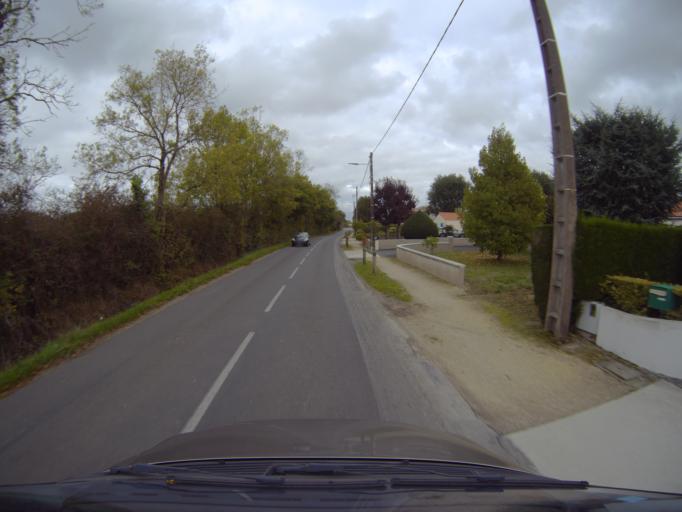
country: FR
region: Pays de la Loire
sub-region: Departement de la Loire-Atlantique
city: Clisson
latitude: 47.1009
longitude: -1.2684
